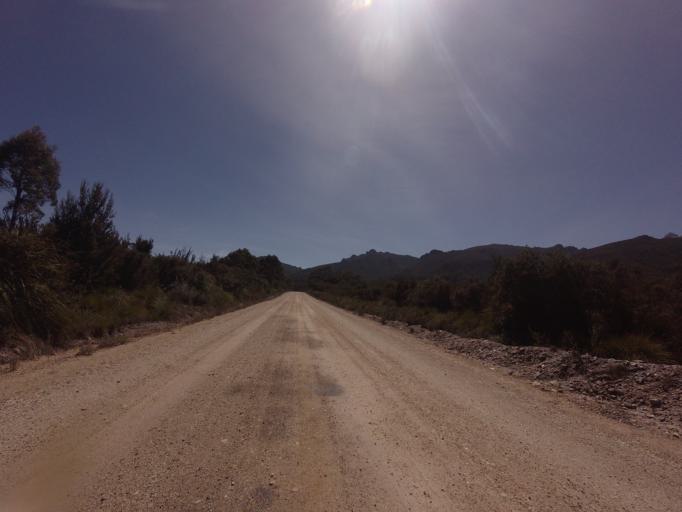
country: AU
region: Tasmania
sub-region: Huon Valley
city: Geeveston
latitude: -42.9630
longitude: 146.3608
